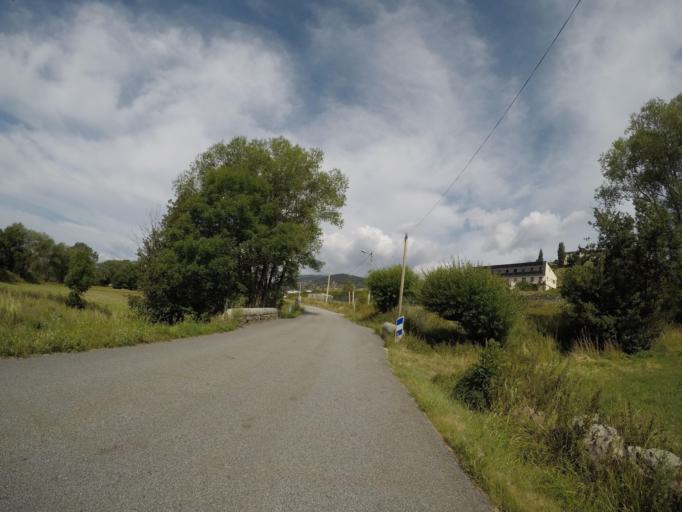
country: ES
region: Catalonia
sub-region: Provincia de Girona
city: Llivia
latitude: 42.4956
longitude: 2.0411
